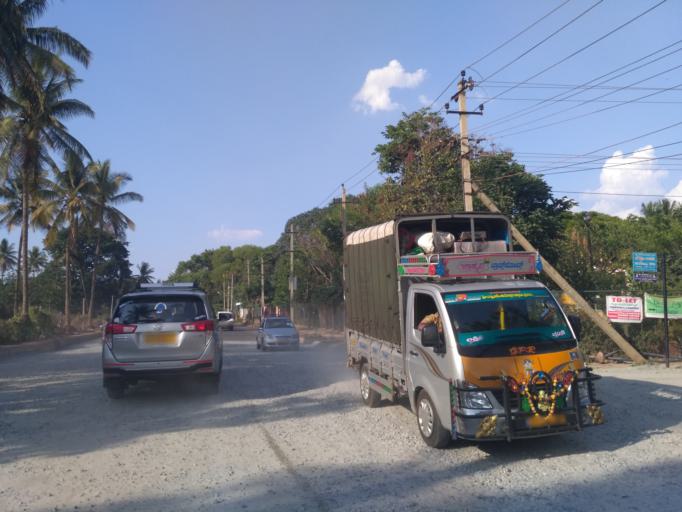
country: IN
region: Karnataka
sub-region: Bangalore Urban
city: Yelahanka
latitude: 13.0463
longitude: 77.5416
